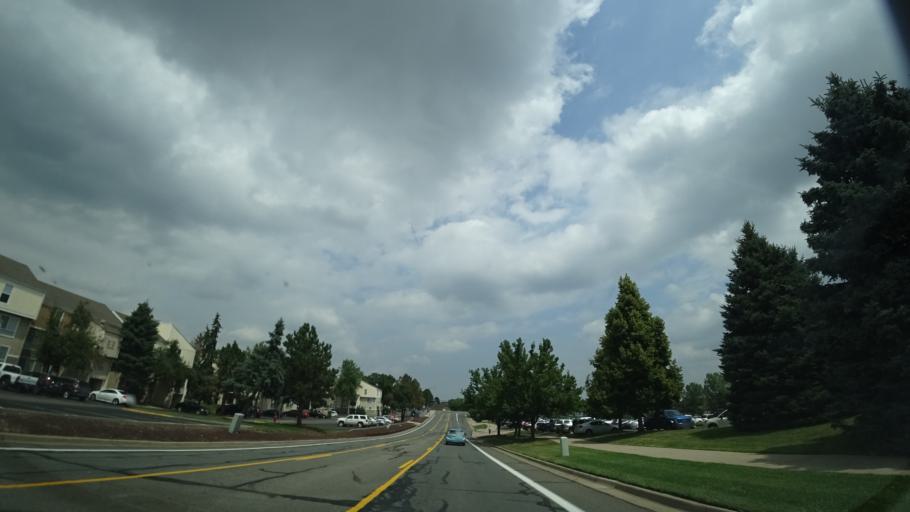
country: US
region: Colorado
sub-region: Jefferson County
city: West Pleasant View
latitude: 39.7209
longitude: -105.1351
